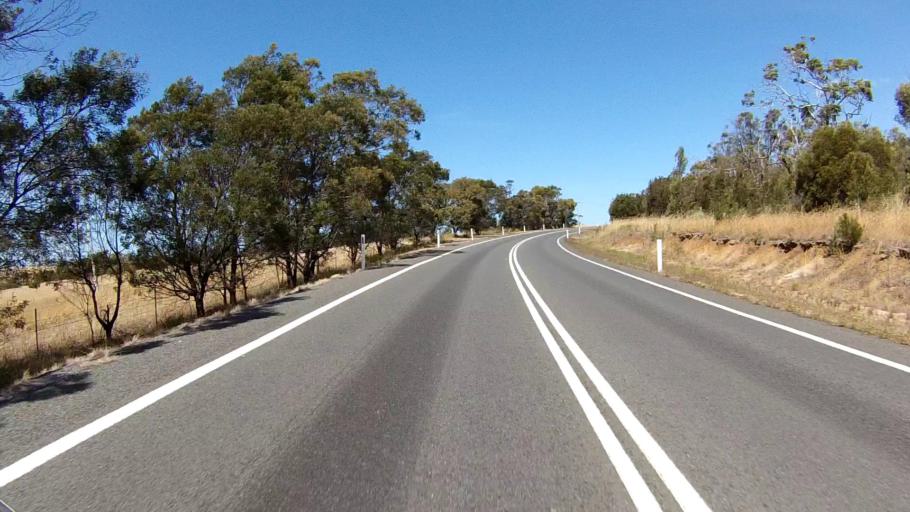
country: AU
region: Tasmania
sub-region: Break O'Day
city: St Helens
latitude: -42.0779
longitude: 148.0684
